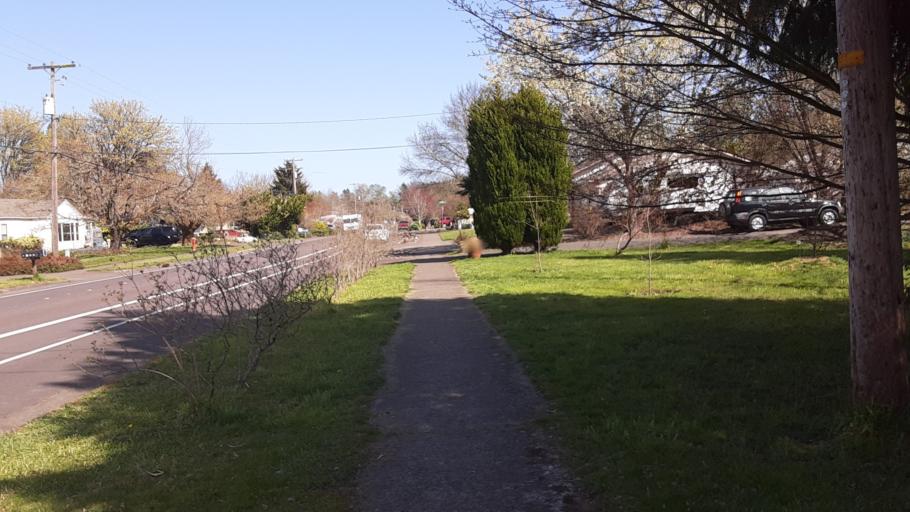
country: US
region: Oregon
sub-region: Benton County
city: Corvallis
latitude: 44.5367
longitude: -123.2611
